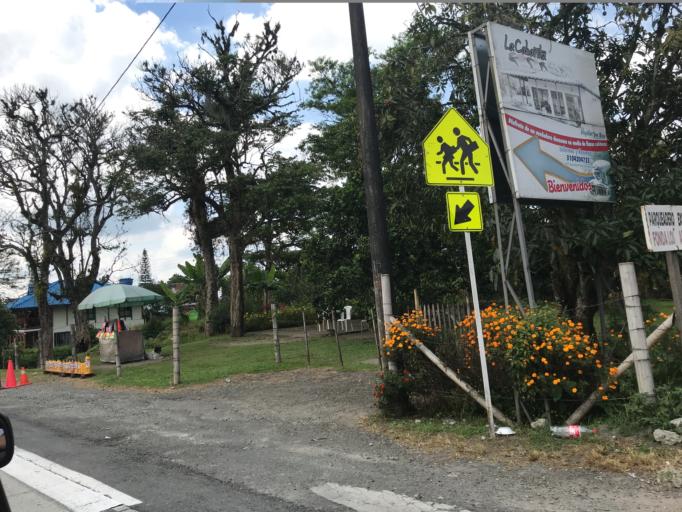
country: CO
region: Quindio
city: Armenia
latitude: 4.5000
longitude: -75.6729
